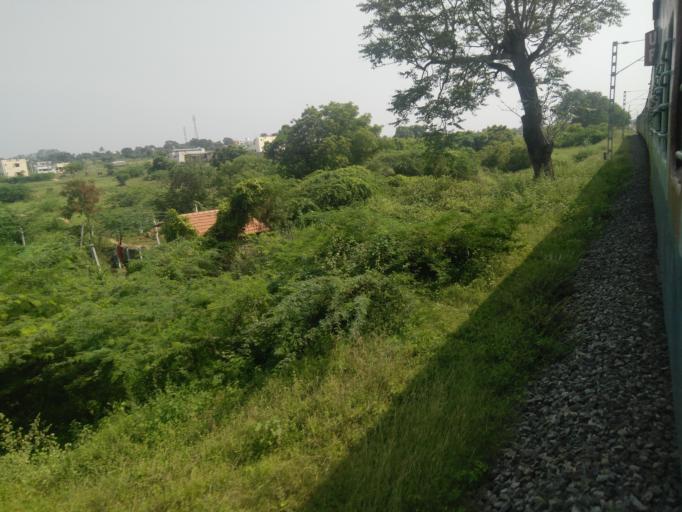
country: IN
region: Tamil Nadu
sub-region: Coimbatore
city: Mettupalayam
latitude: 11.2783
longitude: 76.9418
